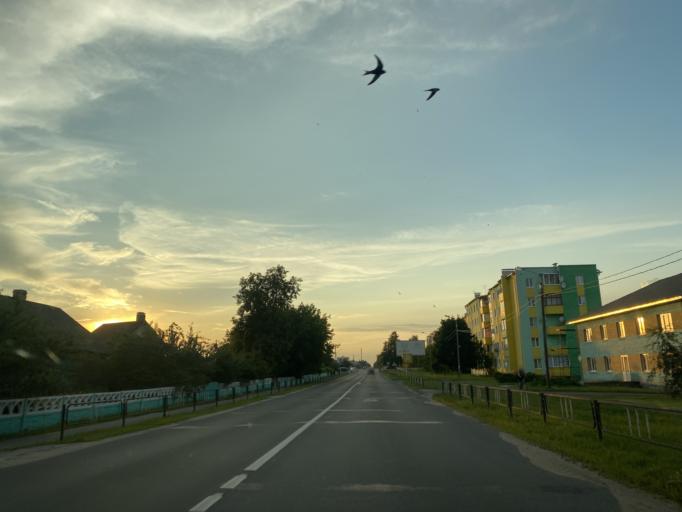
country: BY
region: Brest
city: Ivatsevichy
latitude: 52.7065
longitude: 25.3569
